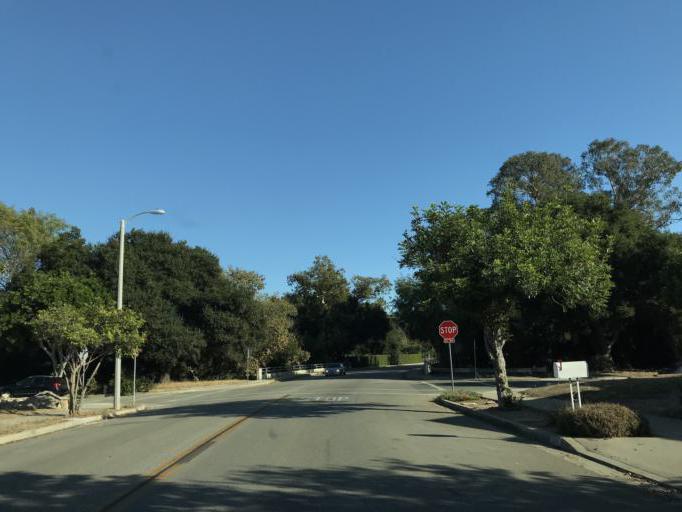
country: US
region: California
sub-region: Santa Barbara County
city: Goleta
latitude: 34.4579
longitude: -119.8110
